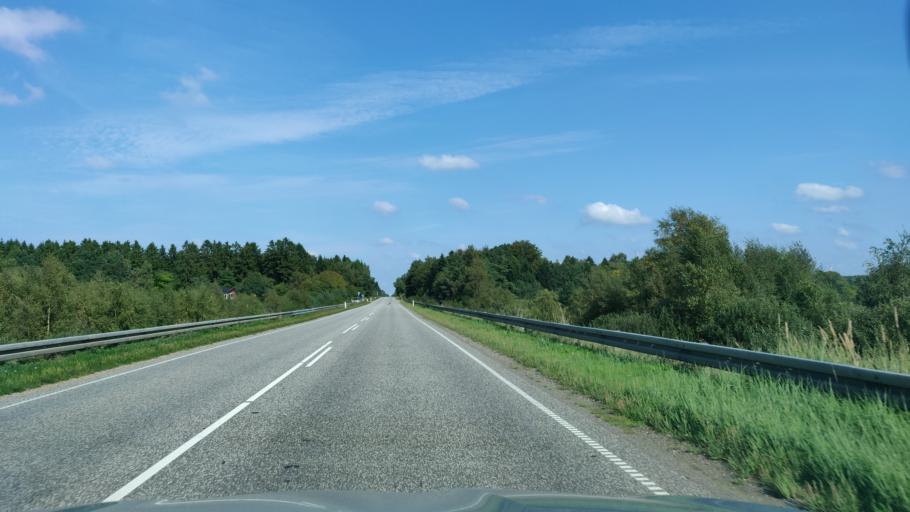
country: DK
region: Central Jutland
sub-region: Herning Kommune
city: Sunds
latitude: 56.3580
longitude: 8.9738
